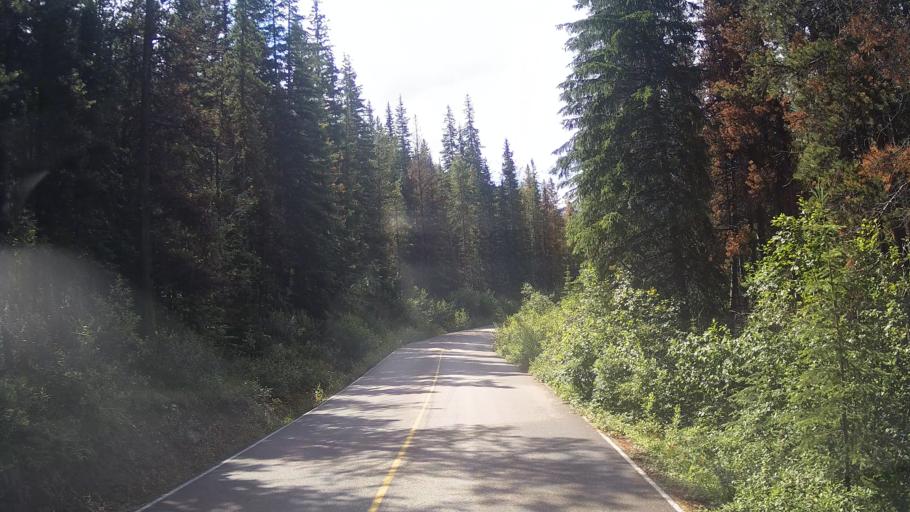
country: CA
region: Alberta
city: Jasper Park Lodge
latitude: 52.7535
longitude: -118.0446
